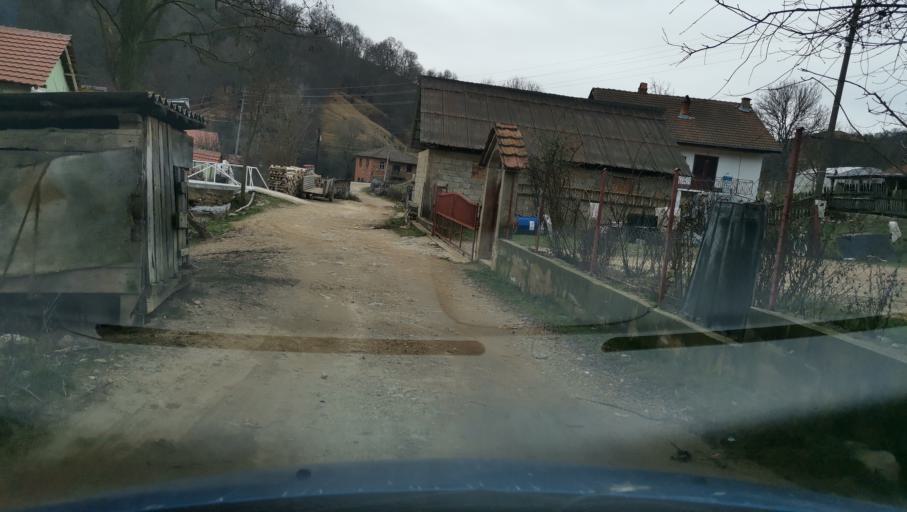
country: MK
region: Berovo
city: Berovo
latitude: 41.5909
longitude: 22.9186
